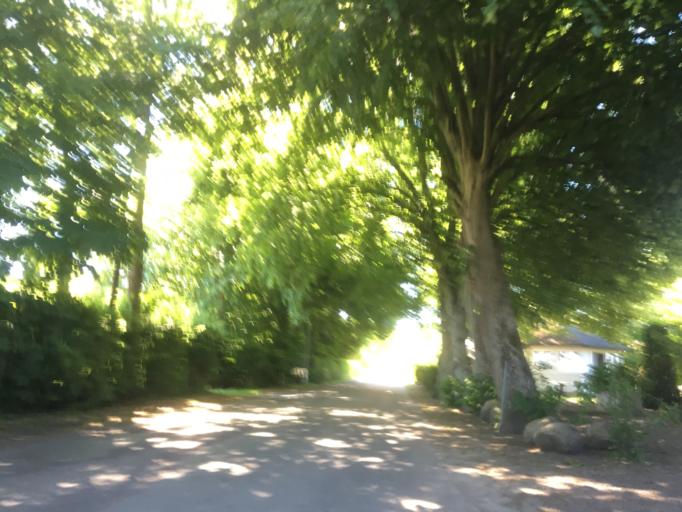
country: SE
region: Skane
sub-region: Helsingborg
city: Rydeback
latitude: 55.9132
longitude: 12.6891
